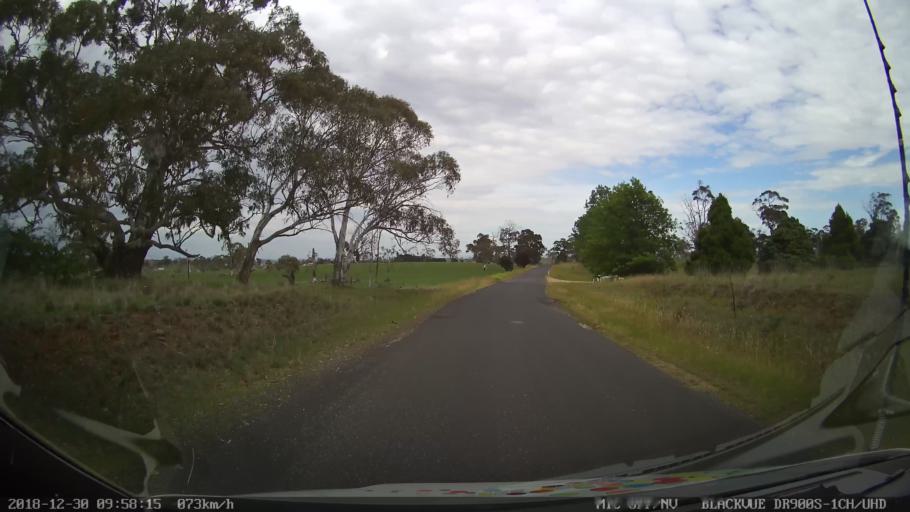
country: AU
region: New South Wales
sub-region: Cooma-Monaro
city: Cooma
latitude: -36.5225
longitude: 149.2286
